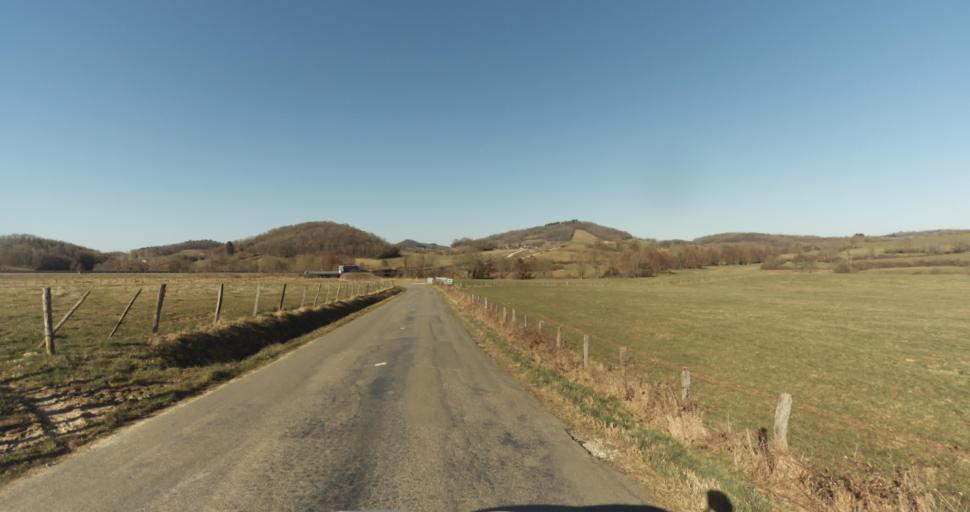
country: FR
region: Franche-Comte
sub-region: Departement du Jura
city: Montmorot
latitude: 46.6965
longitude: 5.5333
